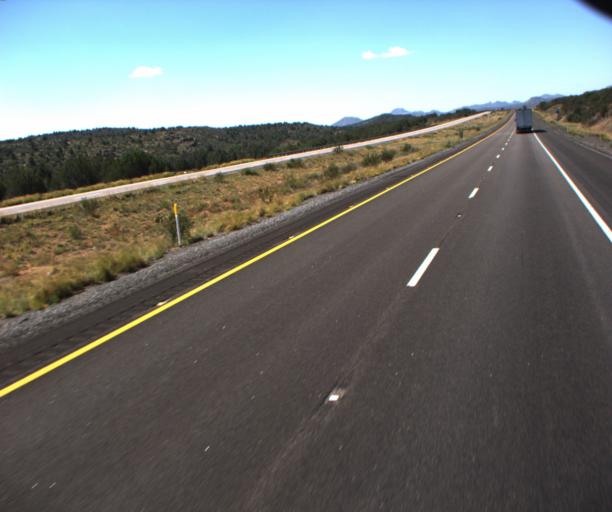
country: US
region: Arizona
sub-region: Mohave County
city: Peach Springs
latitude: 35.1999
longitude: -113.3041
